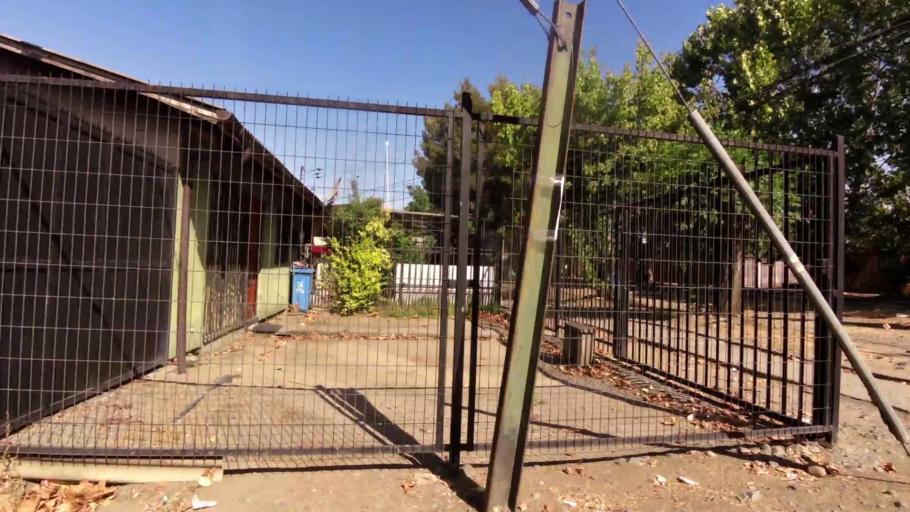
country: CL
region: Maule
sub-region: Provincia de Talca
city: Talca
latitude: -35.4335
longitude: -71.6684
